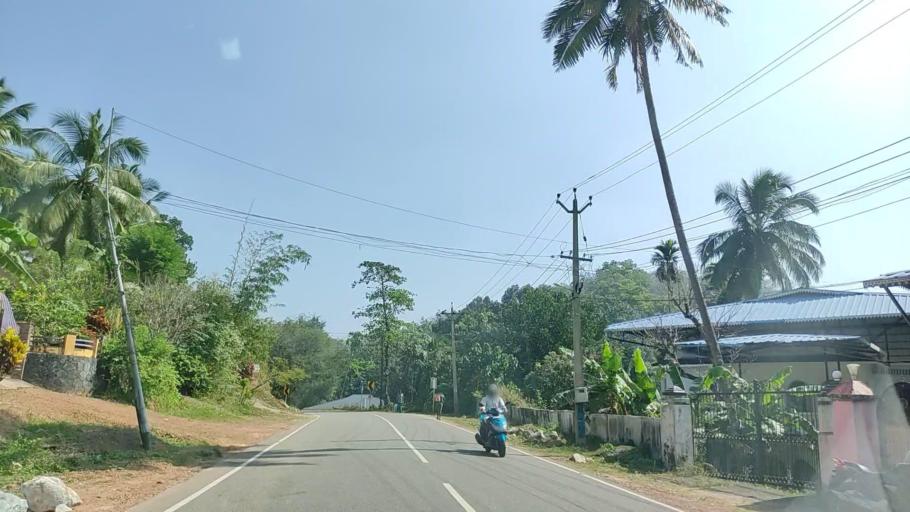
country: IN
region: Kerala
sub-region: Kollam
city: Punalur
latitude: 8.9201
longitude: 77.0576
